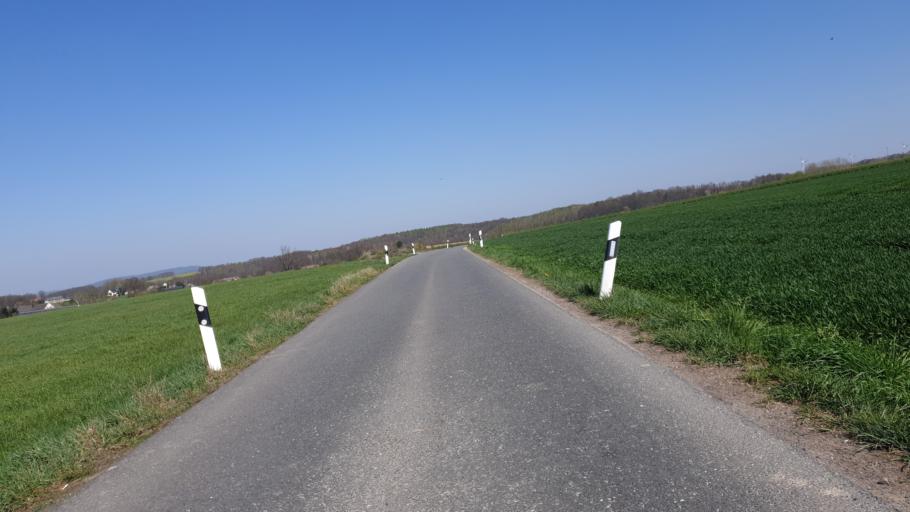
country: DE
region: Saxony
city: Taura
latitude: 50.9296
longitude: 12.8294
